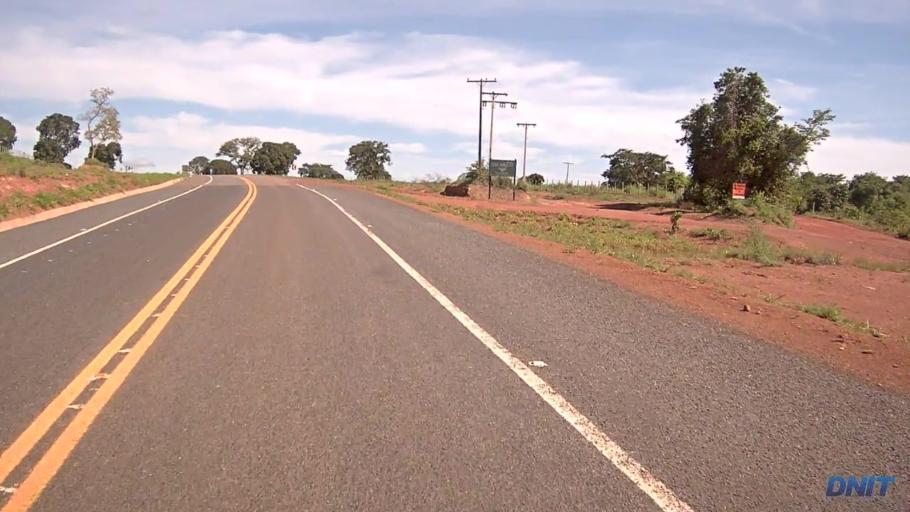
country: BR
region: Goias
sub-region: Sao Miguel Do Araguaia
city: Sao Miguel do Araguaia
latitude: -13.3225
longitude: -50.1577
